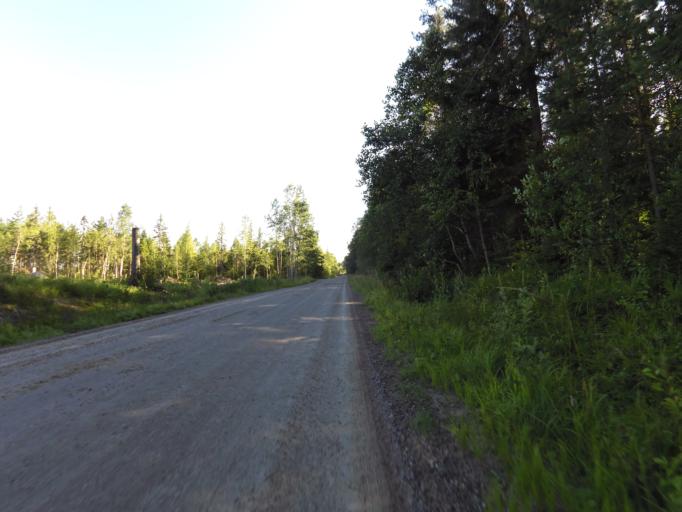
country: SE
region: Gaevleborg
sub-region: Hofors Kommun
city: Hofors
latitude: 60.5797
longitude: 16.2554
